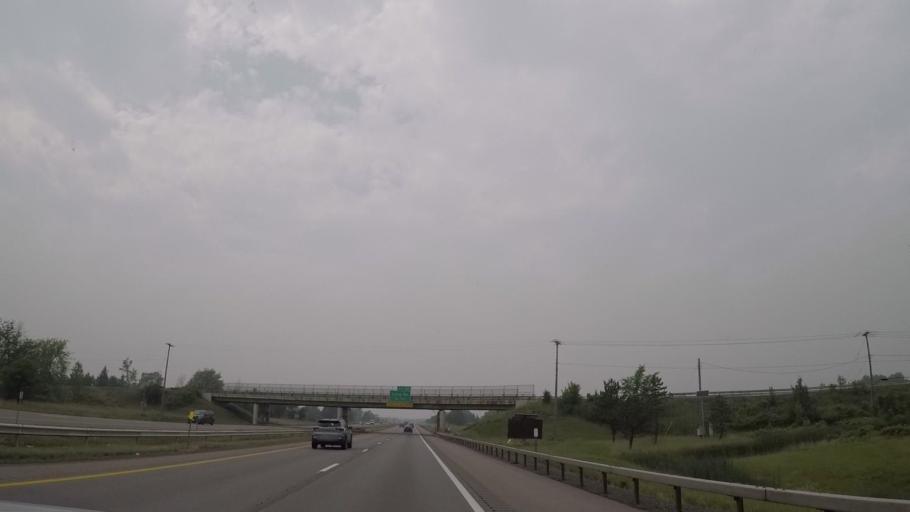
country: US
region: New York
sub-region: Erie County
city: Grandyle Village
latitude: 43.0354
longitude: -78.9836
